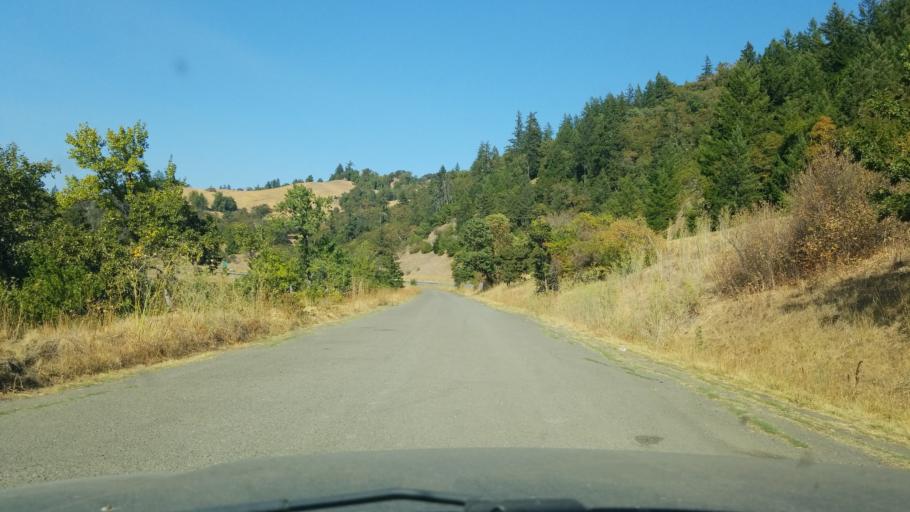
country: US
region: California
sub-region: Humboldt County
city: Redway
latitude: 40.1660
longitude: -123.7844
